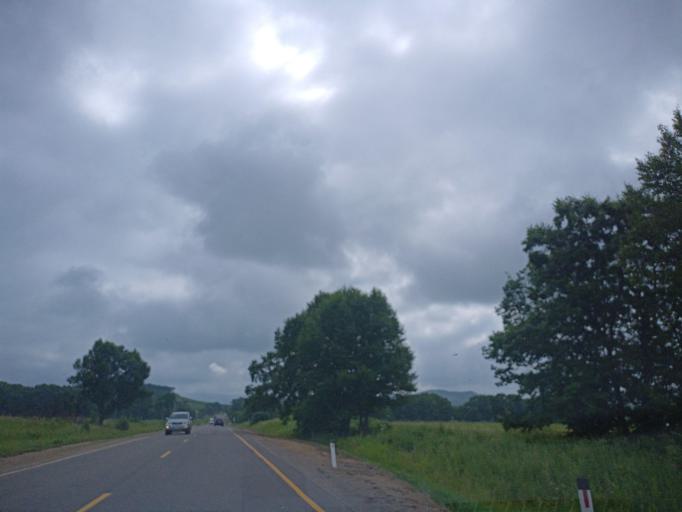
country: RU
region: Primorskiy
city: Dal'nerechensk
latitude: 46.0381
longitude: 133.8743
